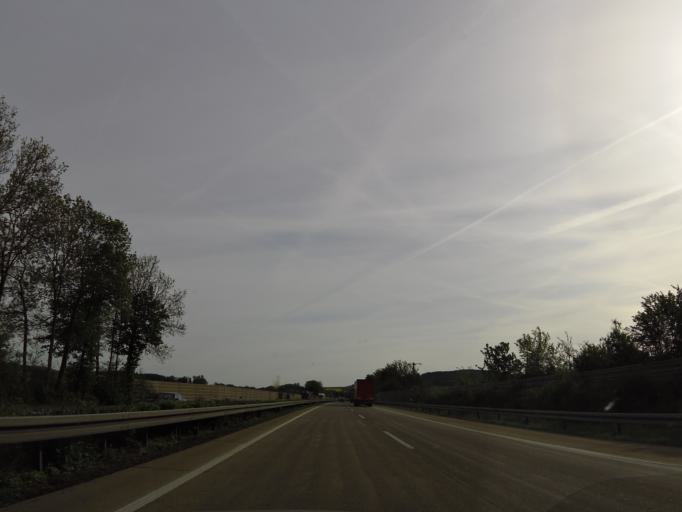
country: DE
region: Lower Saxony
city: Kalefeld
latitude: 51.8084
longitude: 10.0951
